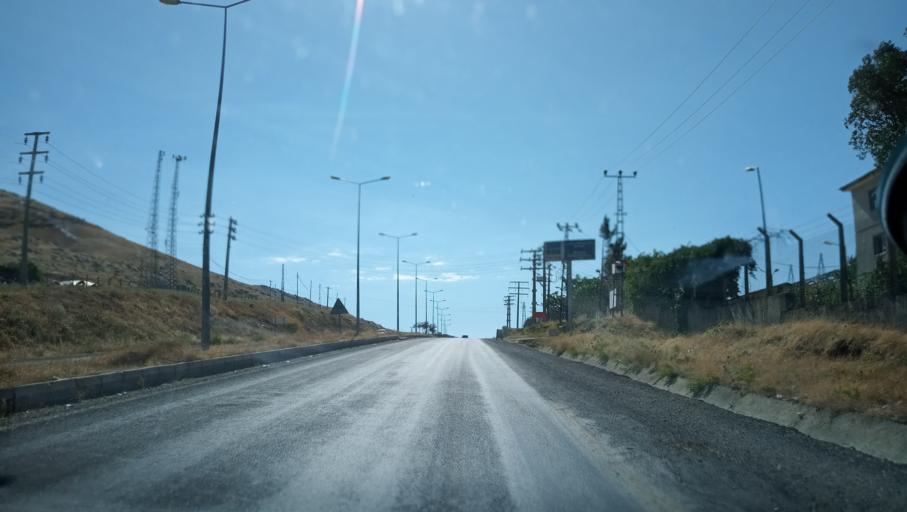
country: TR
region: Diyarbakir
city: Silvan
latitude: 38.1336
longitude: 41.0402
